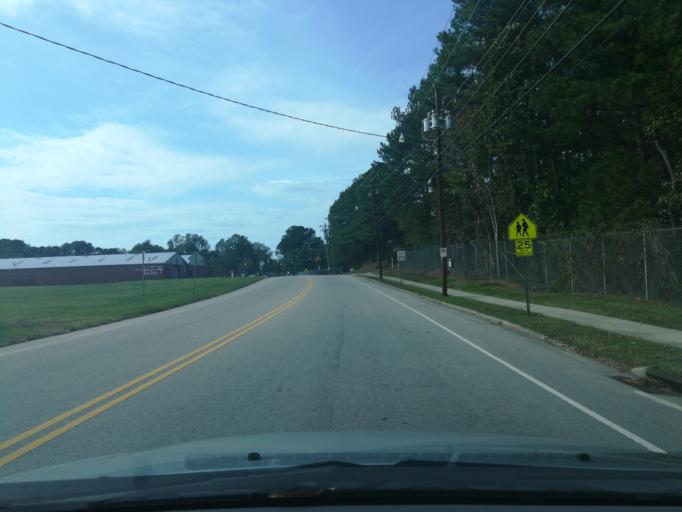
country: US
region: North Carolina
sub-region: Durham County
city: Durham
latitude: 35.9743
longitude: -78.8830
